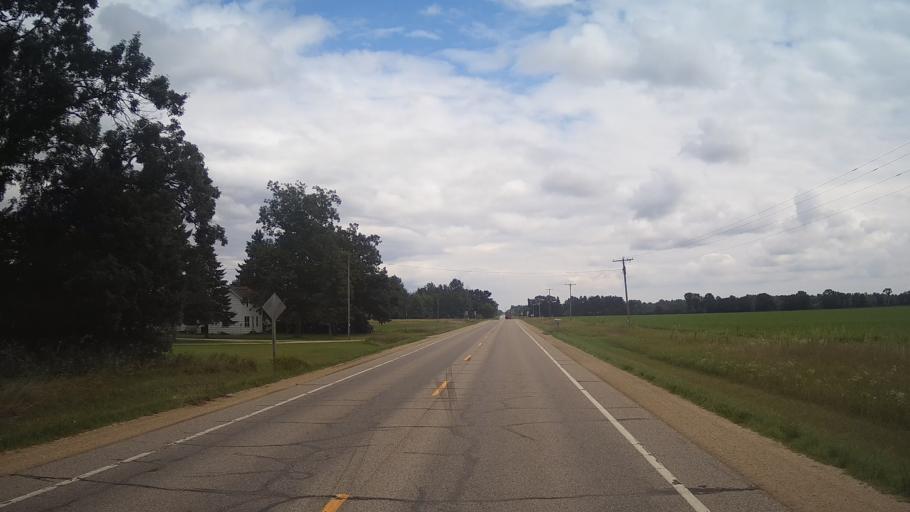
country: US
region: Wisconsin
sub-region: Waushara County
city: Wautoma
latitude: 44.0684
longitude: -89.3562
